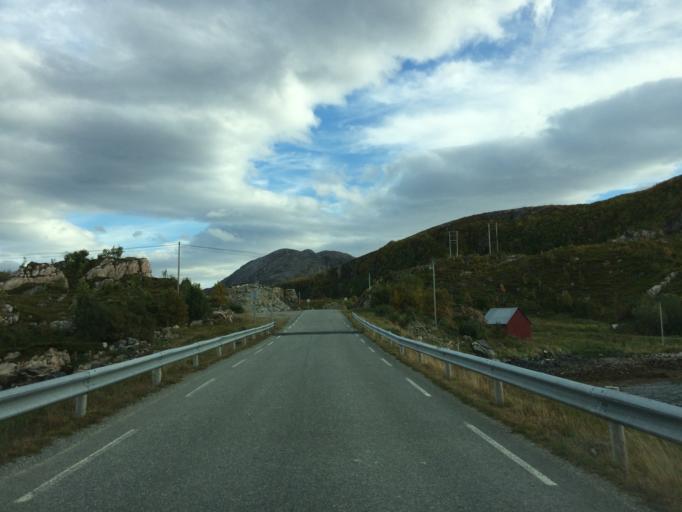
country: NO
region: Troms
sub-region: Lenvik
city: Finnsnes
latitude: 69.6214
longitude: 18.0554
